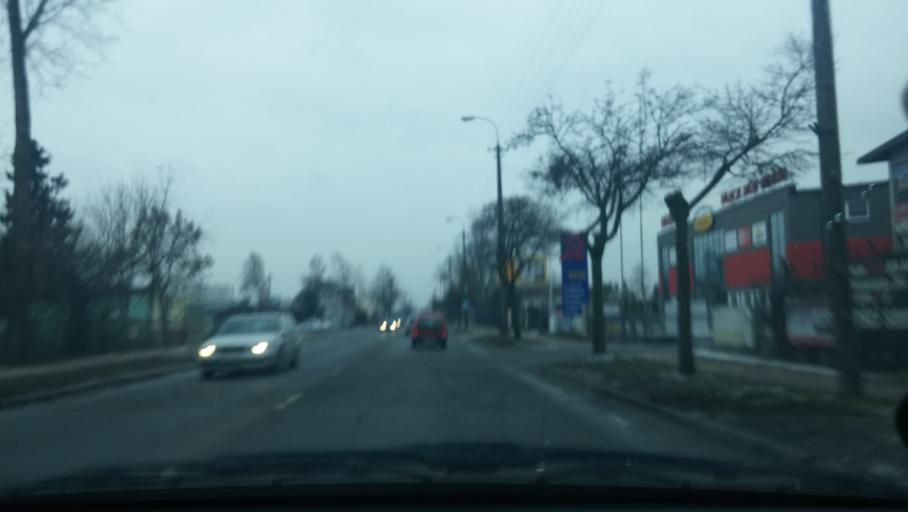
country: PL
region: Masovian Voivodeship
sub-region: Siedlce
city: Siedlce
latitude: 52.1875
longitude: 22.2670
